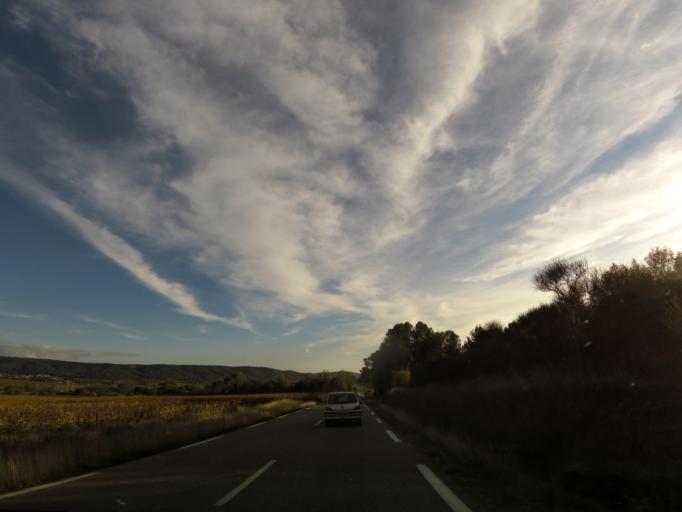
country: FR
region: Languedoc-Roussillon
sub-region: Departement du Gard
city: Ledignan
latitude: 43.9388
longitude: 4.1014
